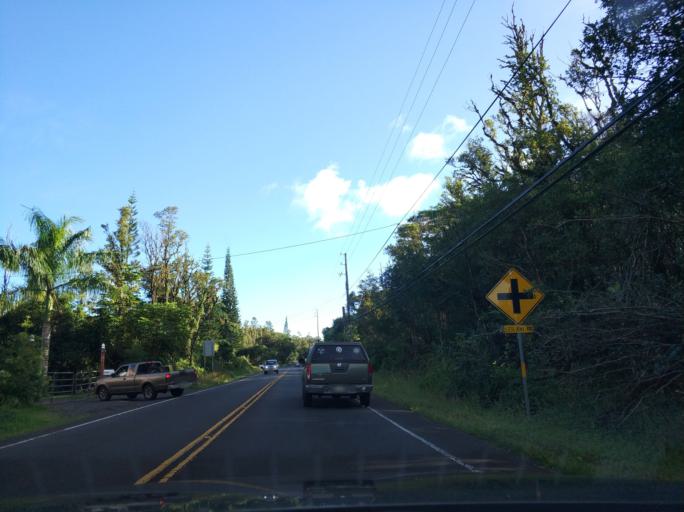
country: US
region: Hawaii
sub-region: Hawaii County
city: Leilani Estates
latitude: 19.4629
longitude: -154.9411
